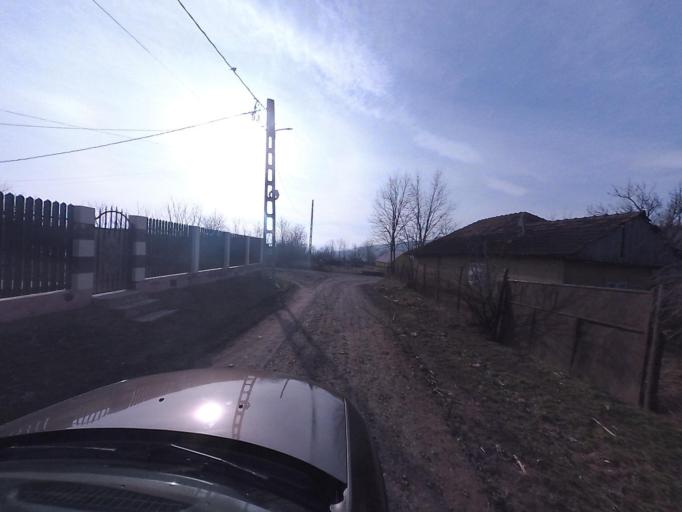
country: RO
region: Vaslui
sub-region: Comuna Solesti
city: Solesti
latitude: 46.8101
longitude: 27.7774
